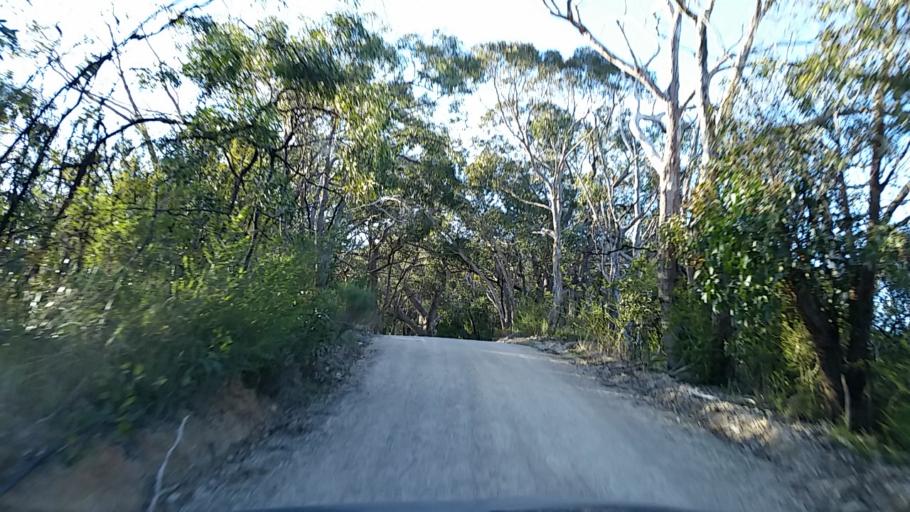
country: AU
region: South Australia
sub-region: Mount Barker
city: Meadows
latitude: -35.2370
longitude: 138.7526
